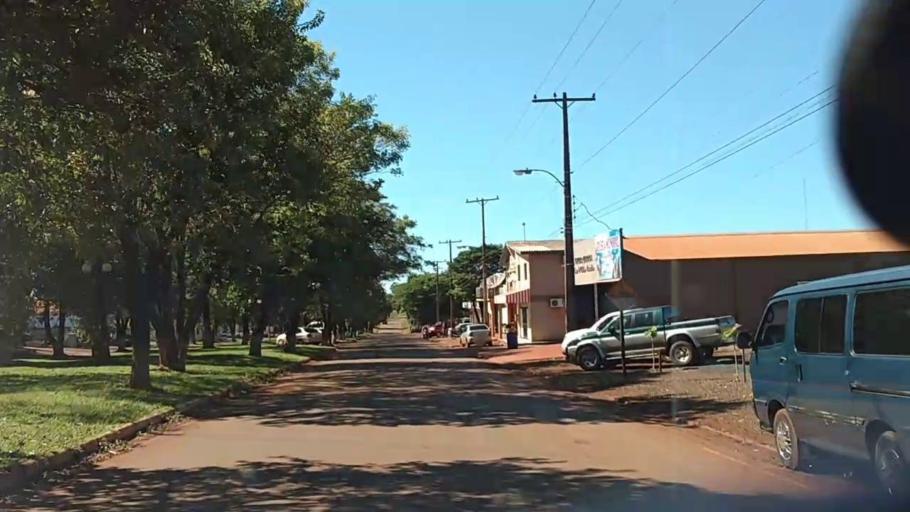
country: PY
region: Alto Parana
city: Naranjal
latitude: -25.9730
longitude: -55.1935
